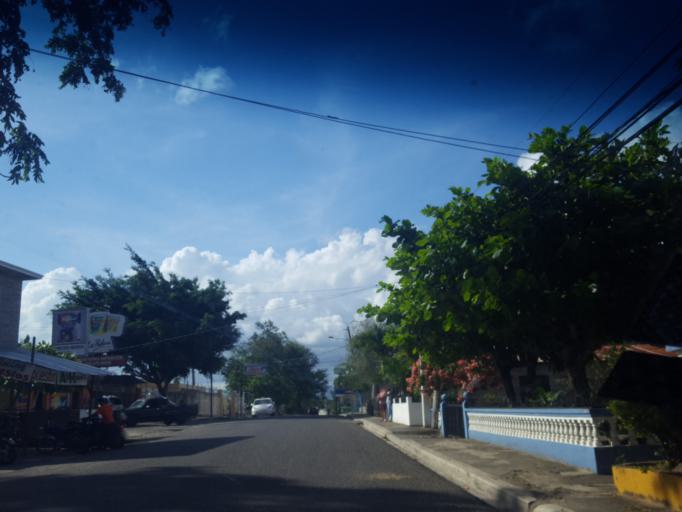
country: DO
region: La Vega
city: Rio Verde Arriba
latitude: 19.3641
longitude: -70.6050
